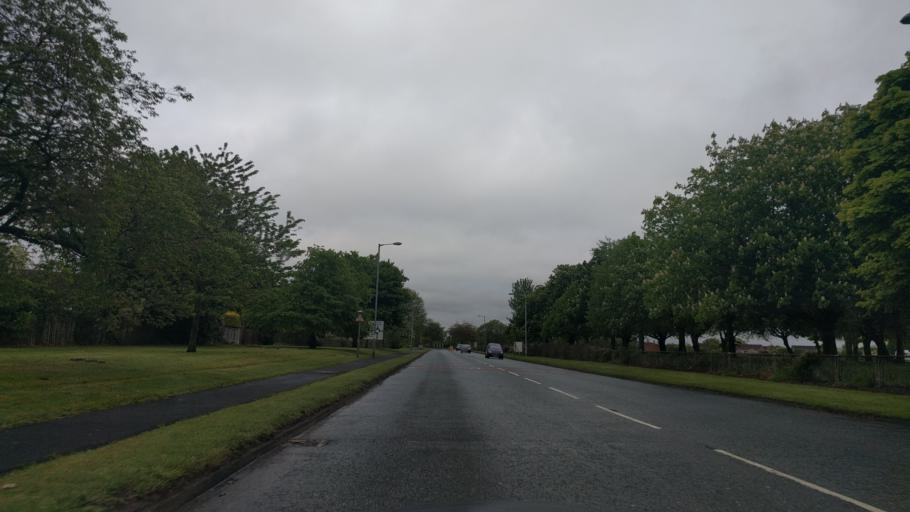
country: GB
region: England
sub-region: Northumberland
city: Morpeth
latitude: 55.1578
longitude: -1.6791
